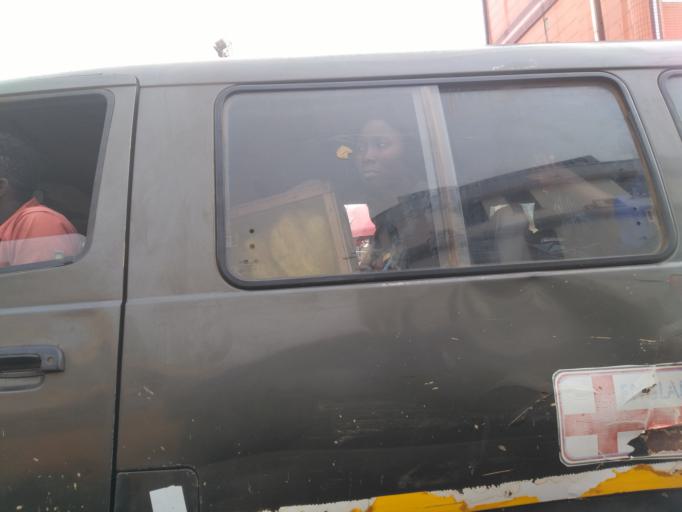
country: GH
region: Ashanti
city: Kumasi
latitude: 6.6950
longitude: -1.6211
